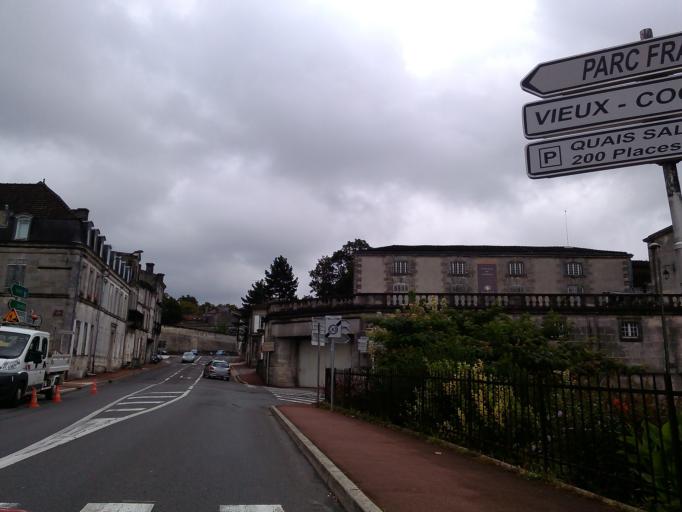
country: FR
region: Poitou-Charentes
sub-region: Departement de la Charente
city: Cognac
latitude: 45.6989
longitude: -0.3300
